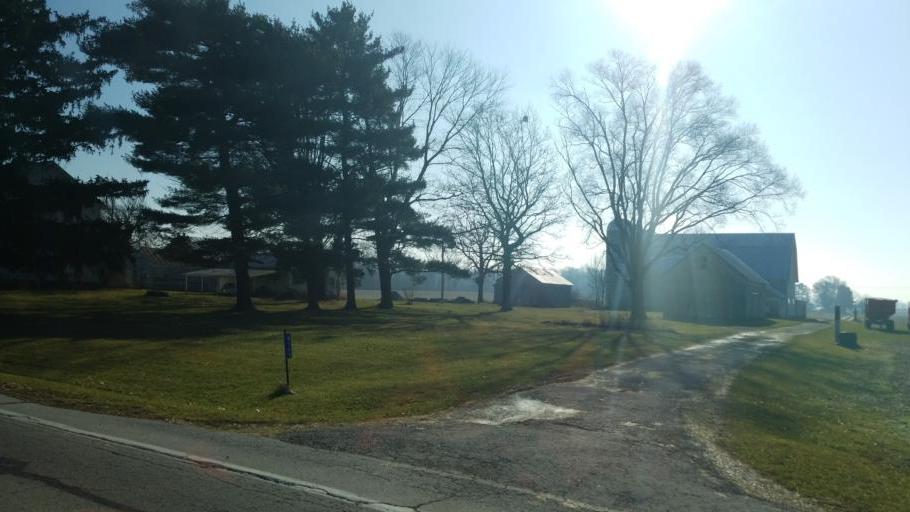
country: US
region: Ohio
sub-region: Seneca County
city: Tiffin
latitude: 41.1243
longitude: -83.1287
